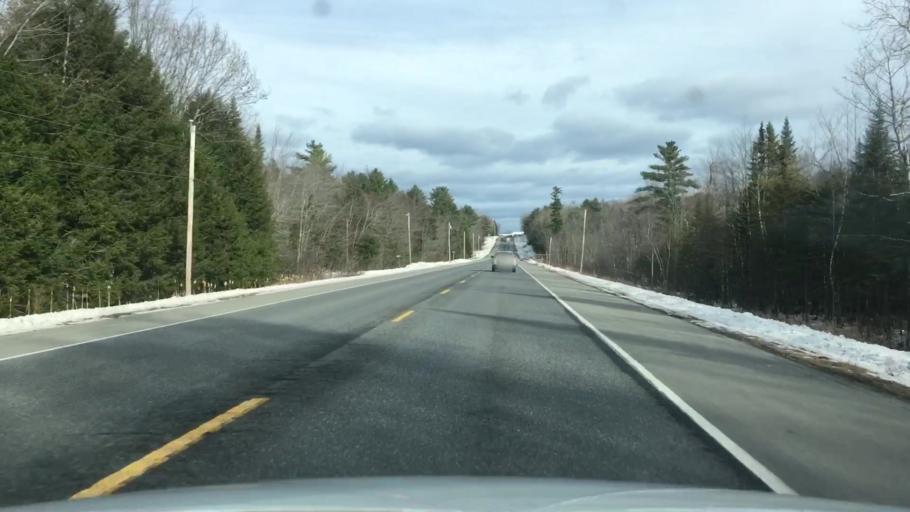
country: US
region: Maine
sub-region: Kennebec County
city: Monmouth
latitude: 44.2631
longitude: -70.0439
